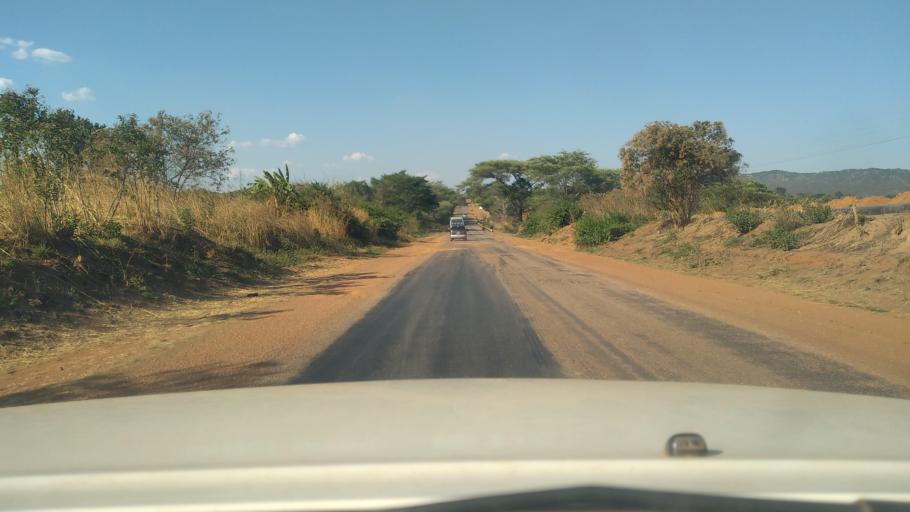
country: ZM
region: Northern
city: Mpika
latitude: -11.7436
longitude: 31.4678
